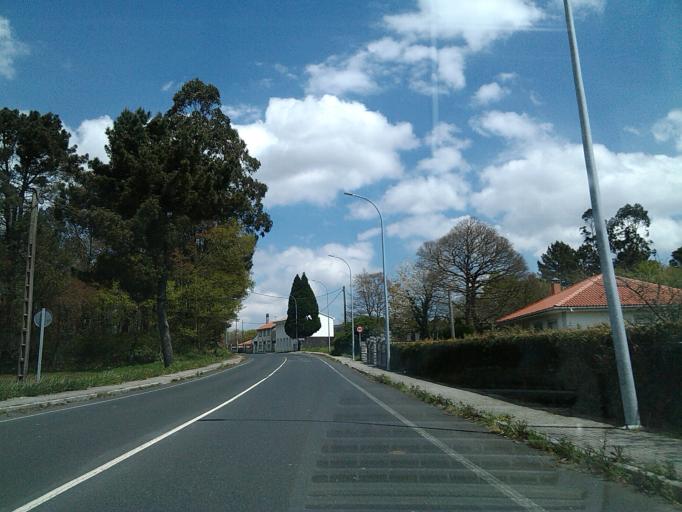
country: ES
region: Galicia
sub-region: Provincia da Coruna
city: Melide
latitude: 42.9521
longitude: -7.9884
